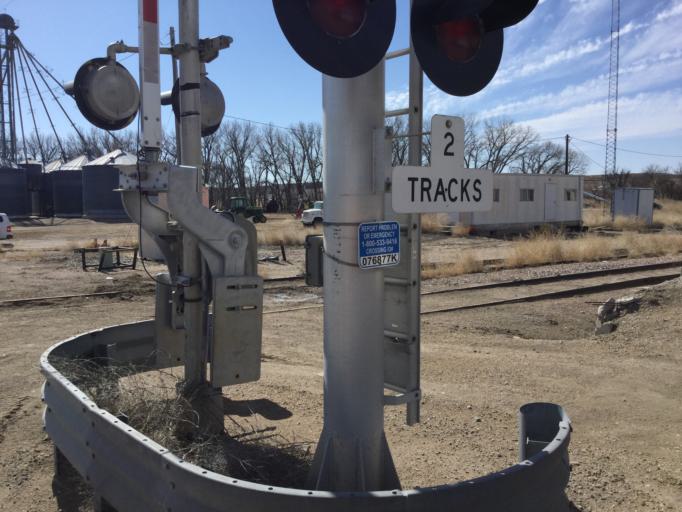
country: US
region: Kansas
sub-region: Rawlins County
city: Atwood
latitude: 39.8233
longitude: -101.0468
